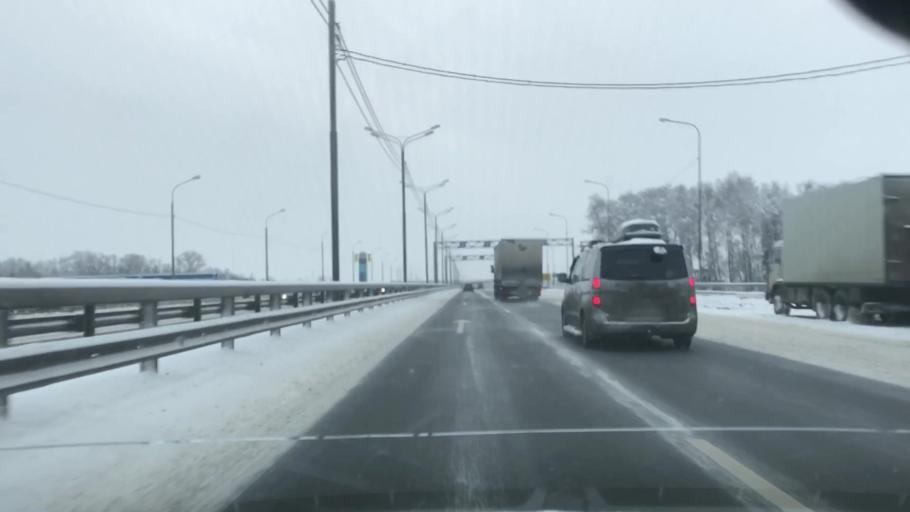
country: RU
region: Moskovskaya
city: Belyye Stolby
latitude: 55.2876
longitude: 37.8540
